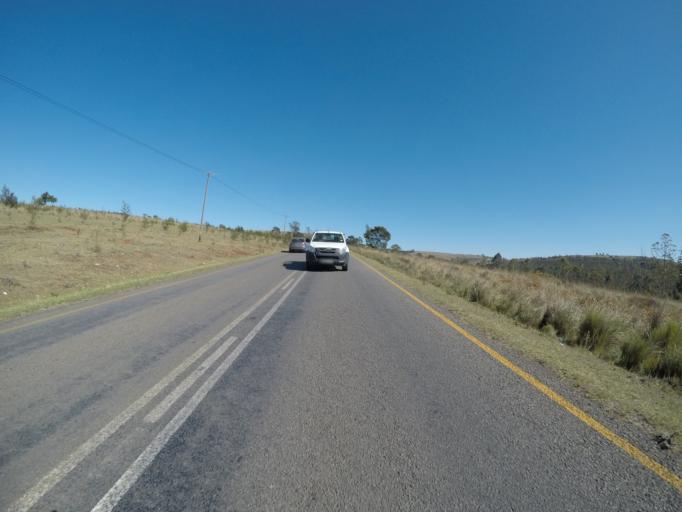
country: ZA
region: Eastern Cape
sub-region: OR Tambo District Municipality
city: Mthatha
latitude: -31.8076
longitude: 28.7627
